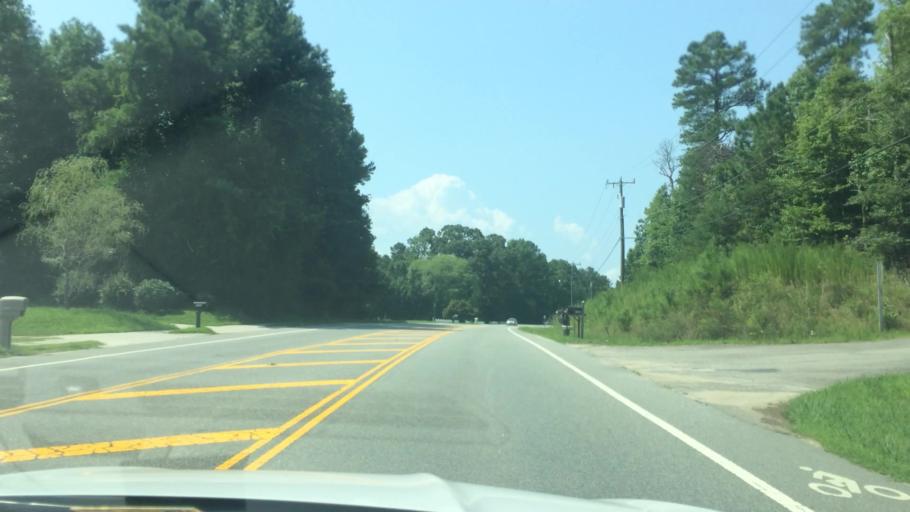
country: US
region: Virginia
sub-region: James City County
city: Williamsburg
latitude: 37.3324
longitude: -76.7842
